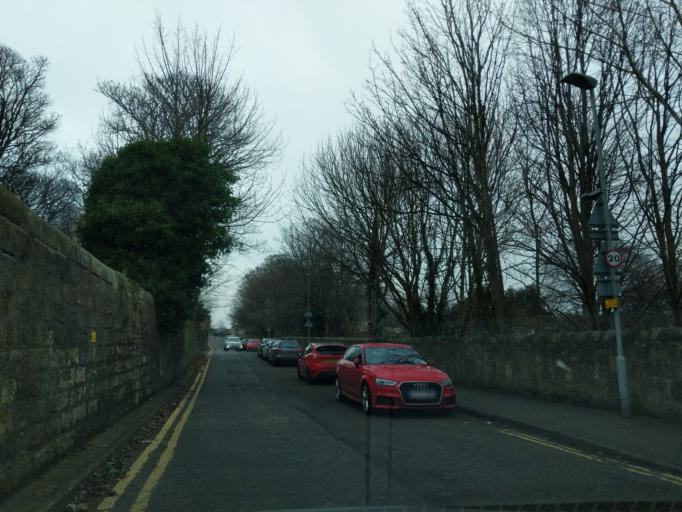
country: GB
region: Scotland
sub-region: Edinburgh
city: Edinburgh
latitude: 55.9691
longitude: -3.1954
